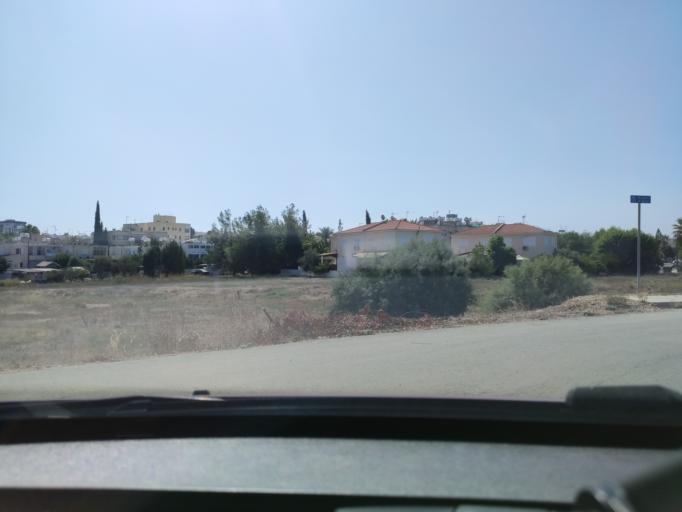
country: CY
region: Lefkosia
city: Geri
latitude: 35.1144
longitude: 33.3744
